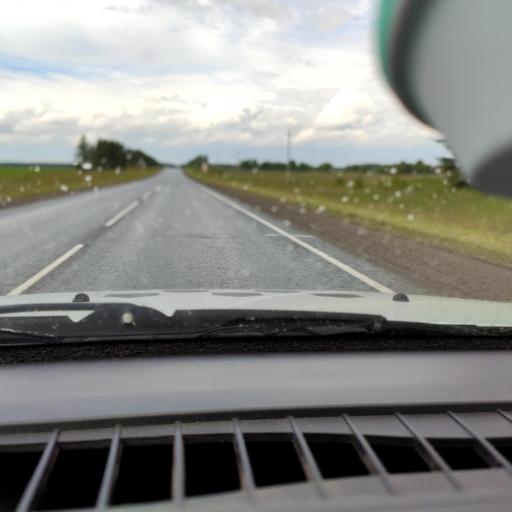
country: RU
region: Perm
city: Orda
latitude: 57.2056
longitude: 56.9260
